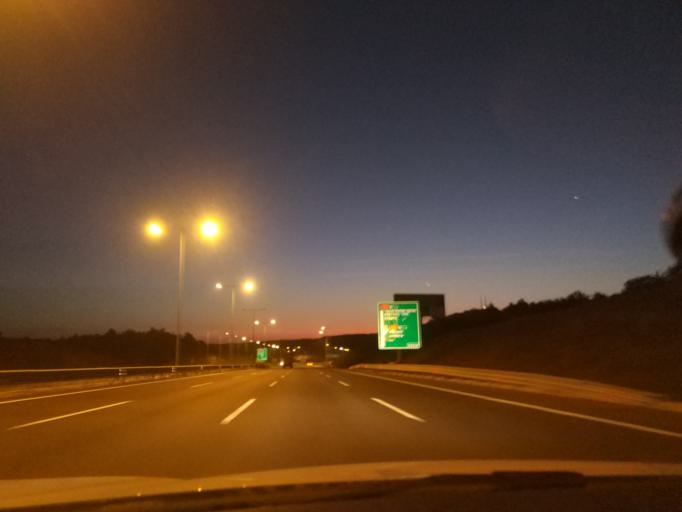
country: TR
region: Istanbul
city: Sancaktepe
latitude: 41.0479
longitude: 29.2643
